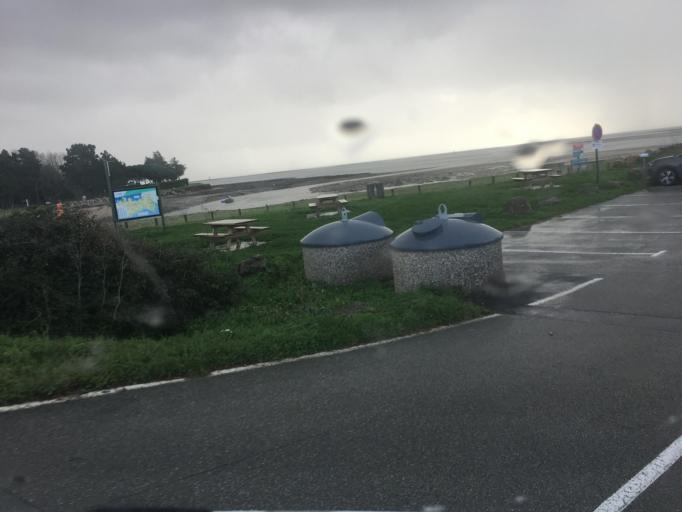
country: FR
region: Brittany
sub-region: Departement du Morbihan
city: Surzur
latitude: 47.5196
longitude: -2.6642
